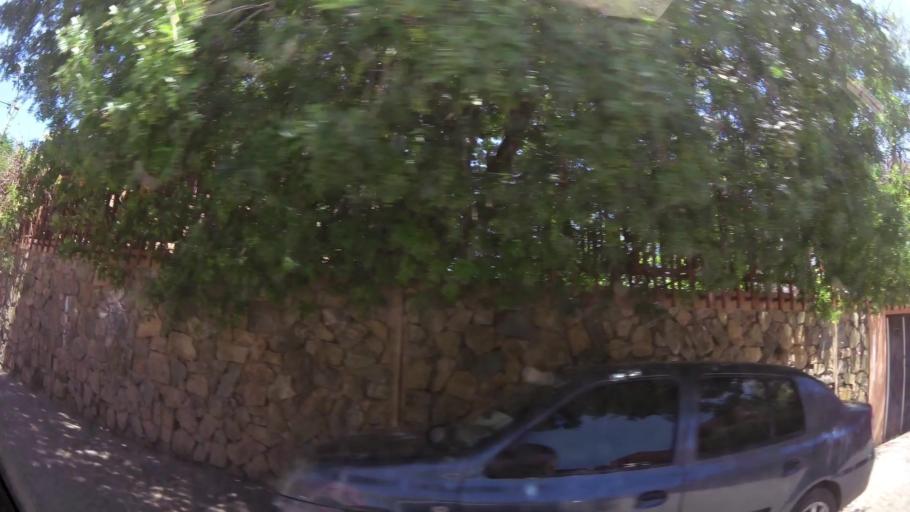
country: MA
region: Marrakech-Tensift-Al Haouz
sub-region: Marrakech
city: Marrakesh
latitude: 31.6524
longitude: -7.9970
